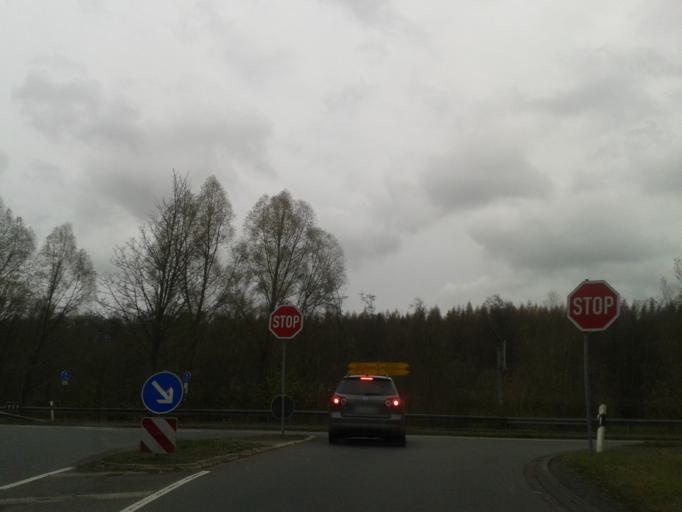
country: DE
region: North Rhine-Westphalia
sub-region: Regierungsbezirk Detmold
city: Blomberg
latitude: 51.9120
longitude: 9.1267
